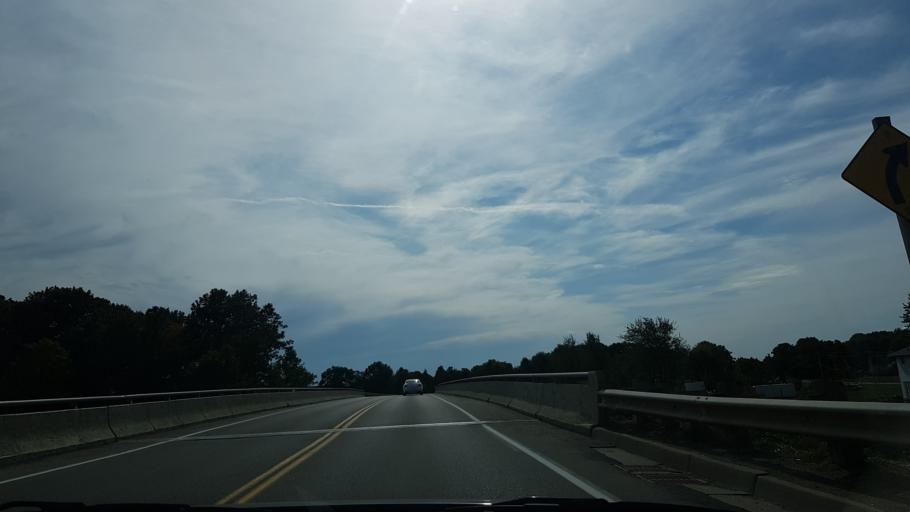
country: CA
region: Ontario
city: Delaware
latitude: 42.9725
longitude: -81.3930
